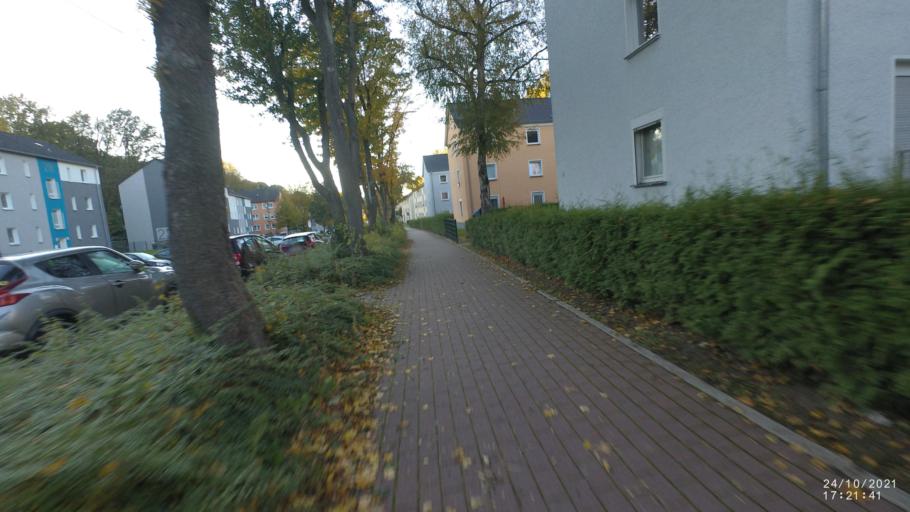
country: DE
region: North Rhine-Westphalia
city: Iserlohn
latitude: 51.3796
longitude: 7.7245
